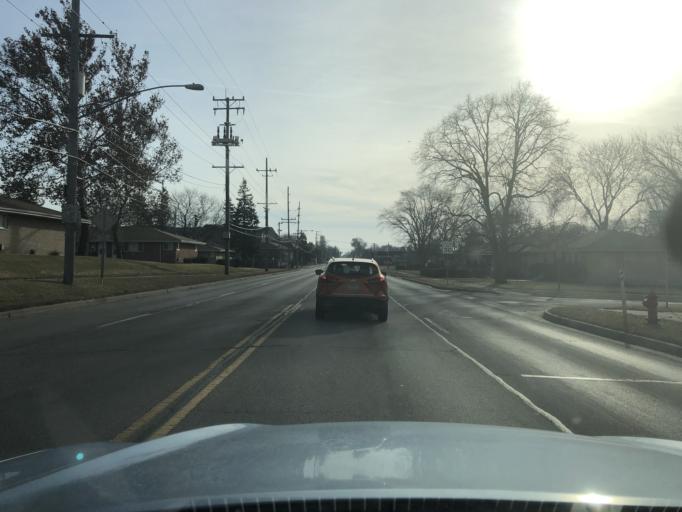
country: US
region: Illinois
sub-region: DuPage County
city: Roselle
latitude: 41.9881
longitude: -88.0803
